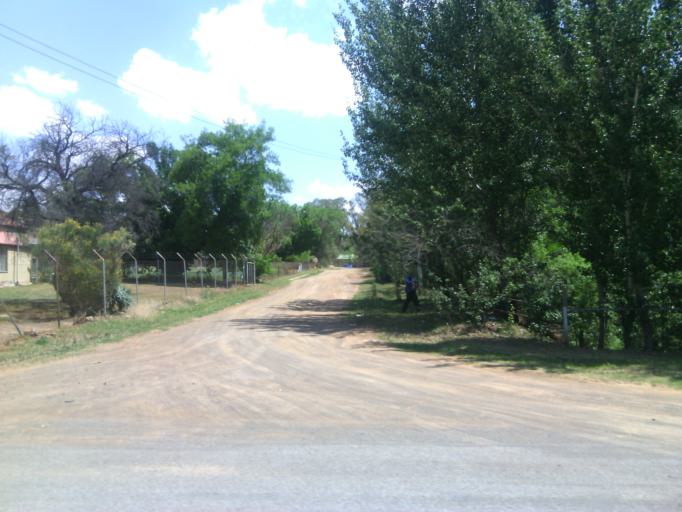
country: ZA
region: Orange Free State
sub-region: Xhariep District Municipality
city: Dewetsdorp
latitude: -29.5871
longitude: 26.6628
